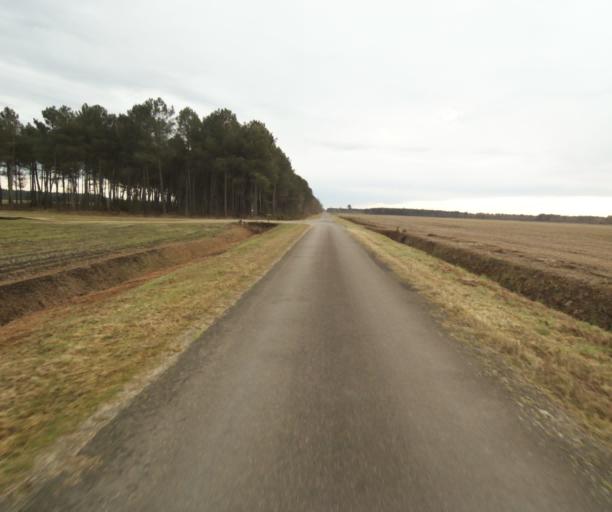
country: FR
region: Aquitaine
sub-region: Departement des Landes
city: Gabarret
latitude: 44.0354
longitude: -0.0689
